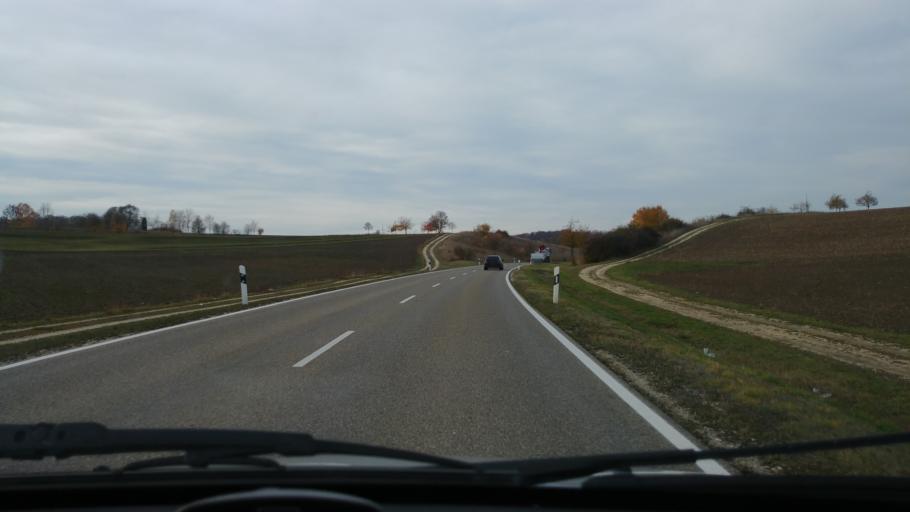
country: DE
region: Bavaria
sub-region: Swabia
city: Zoschingen
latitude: 48.6526
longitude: 10.2770
